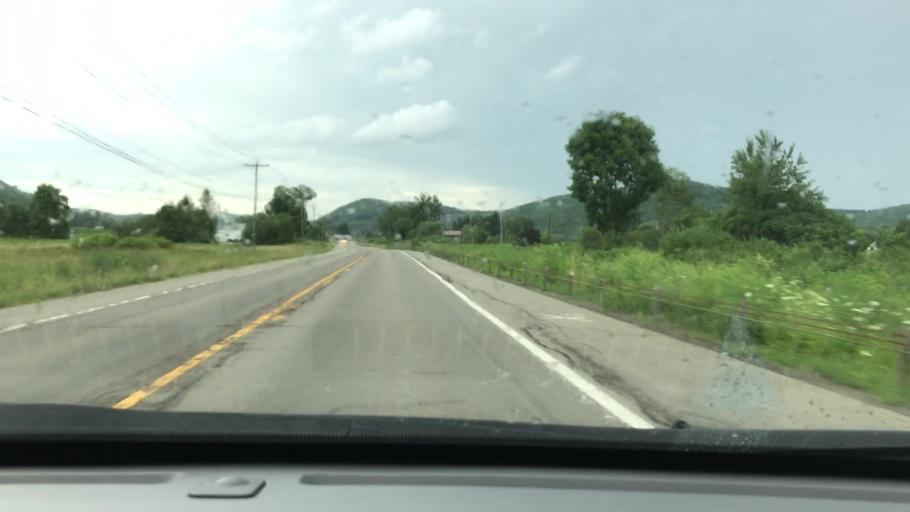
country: US
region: New York
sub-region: Cattaraugus County
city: Salamanca
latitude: 42.2432
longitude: -78.6428
